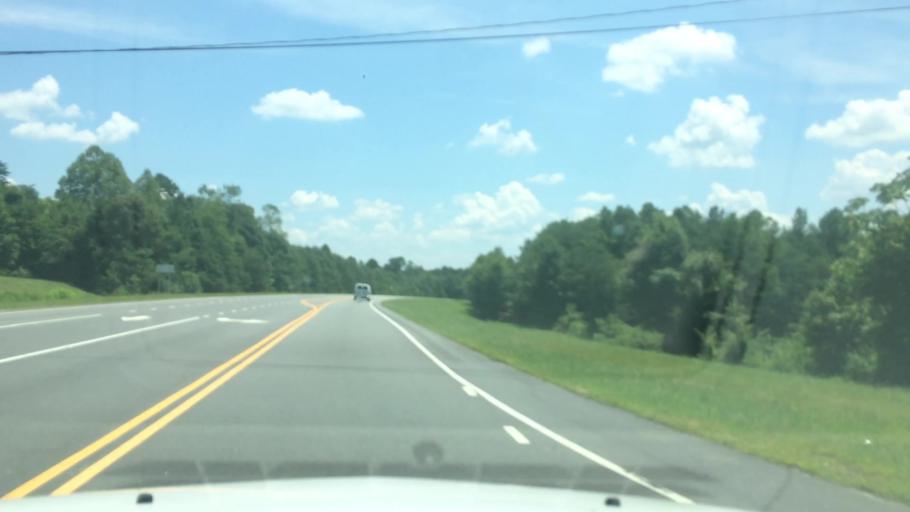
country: US
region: North Carolina
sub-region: Alexander County
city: Stony Point
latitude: 35.8870
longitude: -81.0808
